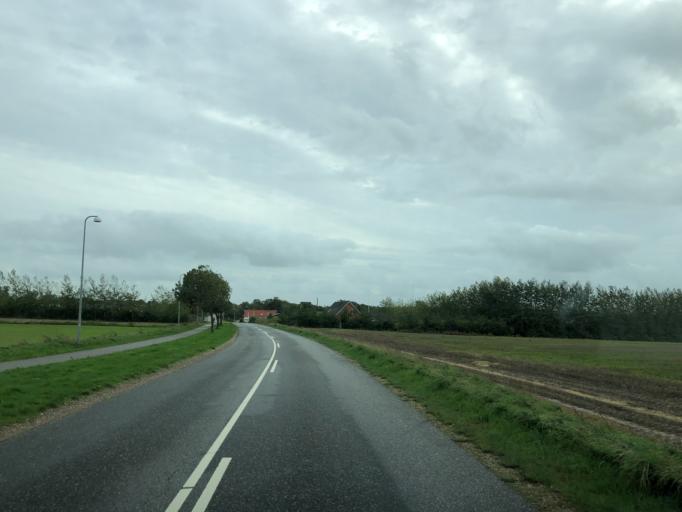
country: DK
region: Central Jutland
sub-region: Herning Kommune
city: Vildbjerg
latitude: 56.1842
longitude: 8.7455
